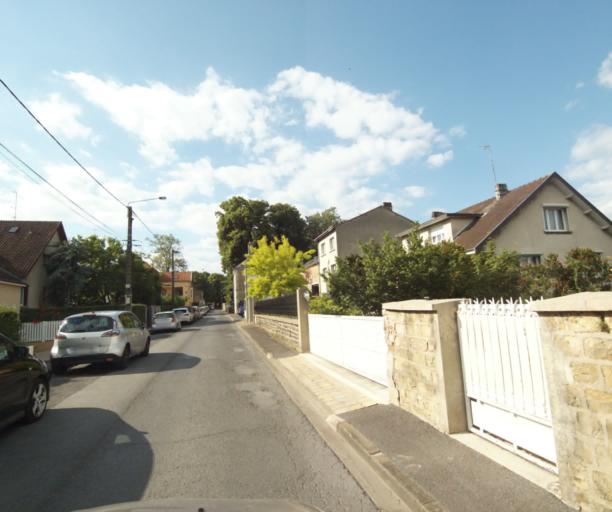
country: FR
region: Champagne-Ardenne
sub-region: Departement des Ardennes
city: Montcy-Notre-Dame
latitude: 49.7758
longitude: 4.7368
